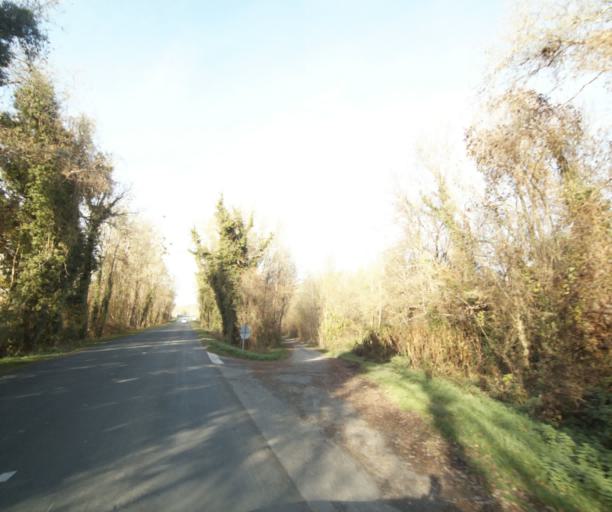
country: FR
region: Poitou-Charentes
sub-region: Departement de la Charente-Maritime
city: Chaniers
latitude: 45.7039
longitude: -0.5287
